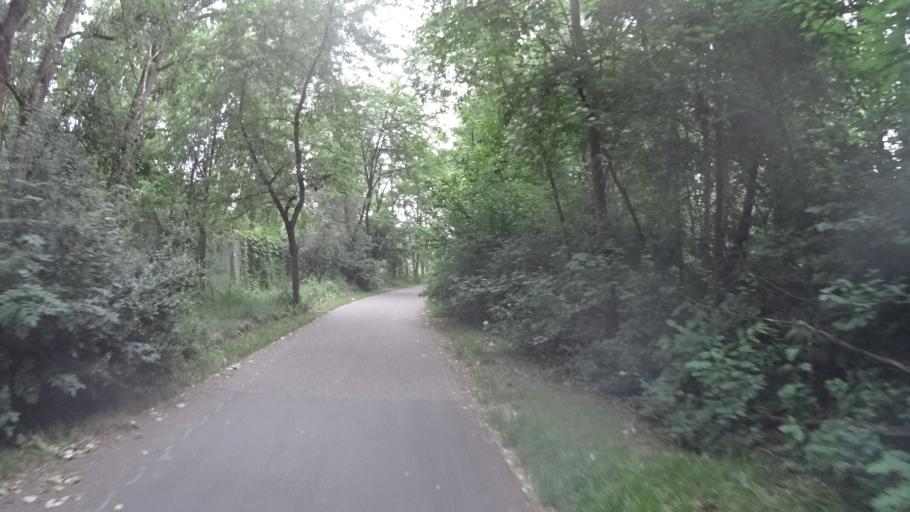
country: DE
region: Bavaria
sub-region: Upper Palatinate
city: Tegernheim
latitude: 49.0194
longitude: 12.1596
